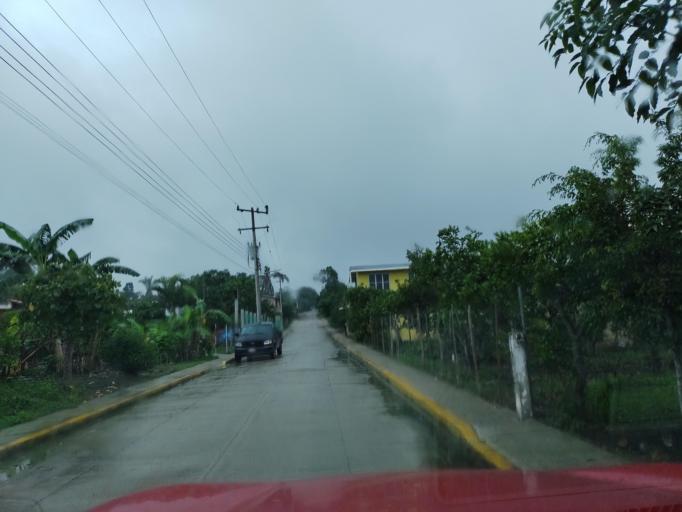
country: MX
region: Veracruz
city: Agua Dulce
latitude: 20.3344
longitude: -97.3242
